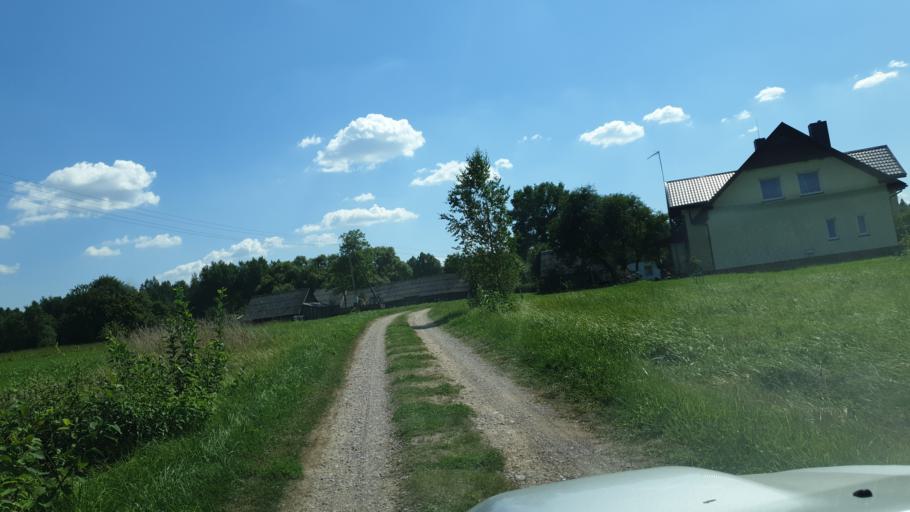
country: LT
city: Sirvintos
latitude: 54.9034
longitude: 24.9108
